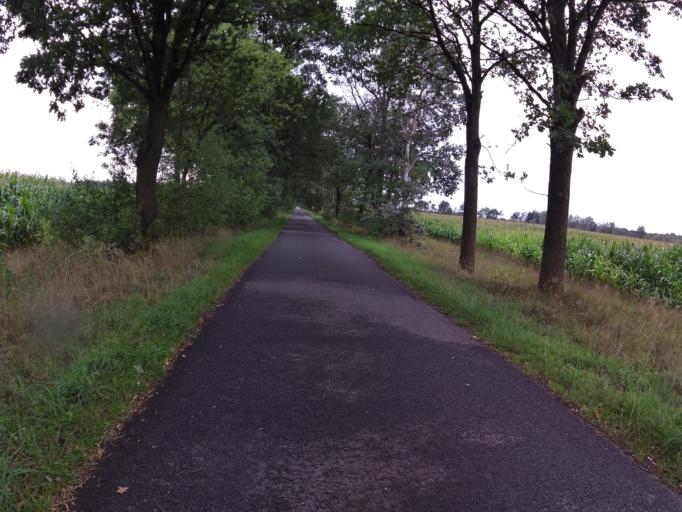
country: DE
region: Lower Saxony
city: Rotenburg
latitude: 53.1438
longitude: 9.4426
